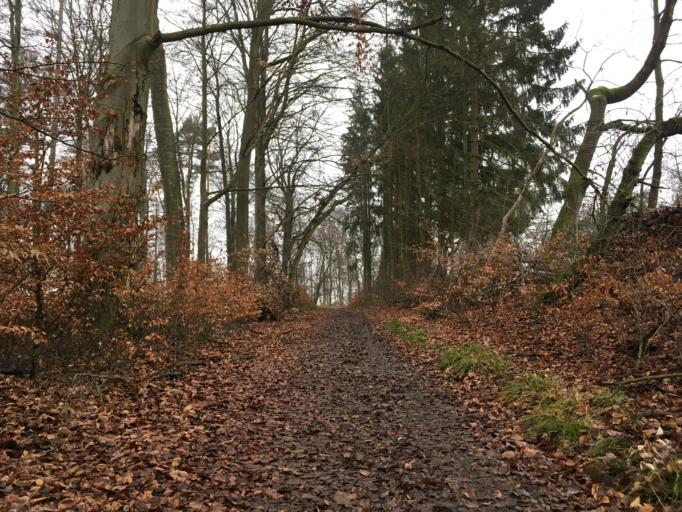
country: DE
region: Baden-Wuerttemberg
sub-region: Karlsruhe Region
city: Konigsbach-Stein
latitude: 48.9487
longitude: 8.5174
